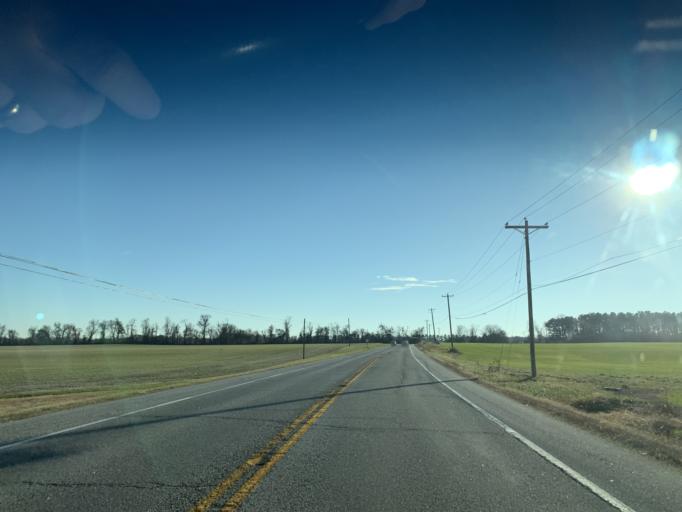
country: US
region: Delaware
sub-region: New Castle County
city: Middletown
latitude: 39.3894
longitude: -75.8715
